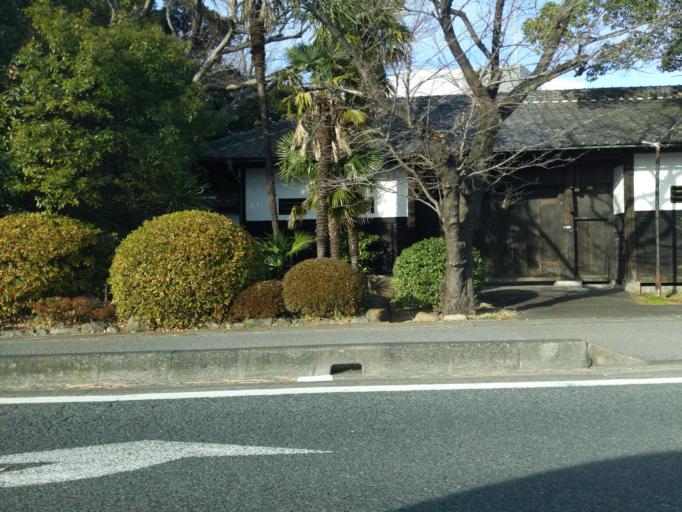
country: JP
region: Saitama
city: Soka
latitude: 35.8360
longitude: 139.7895
